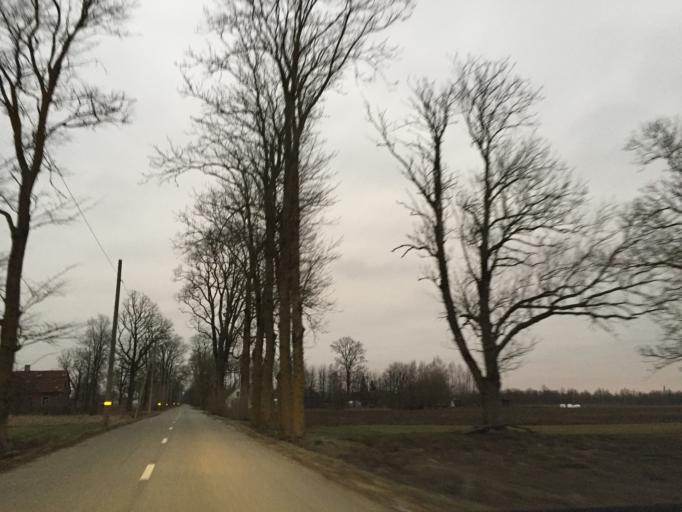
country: LT
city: Zagare
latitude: 56.3355
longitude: 23.2903
